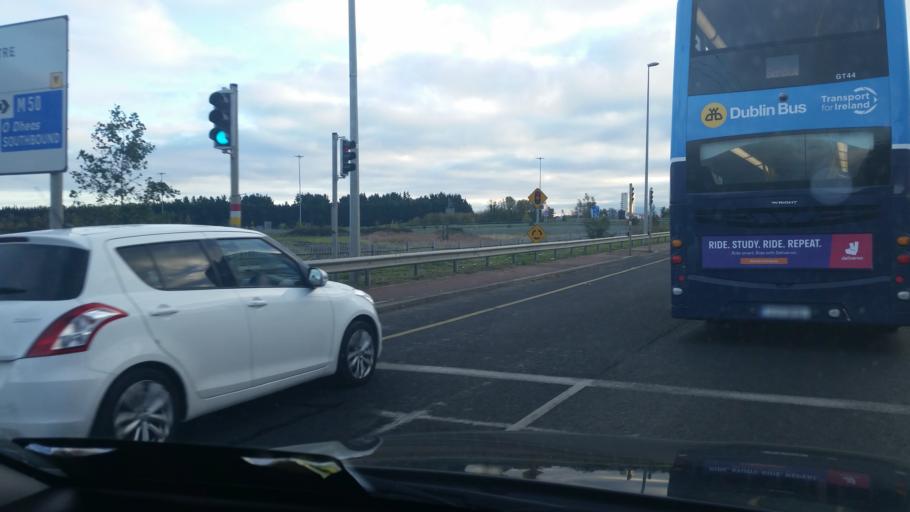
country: IE
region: Leinster
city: Ballymun
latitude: 53.4115
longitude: -6.2654
